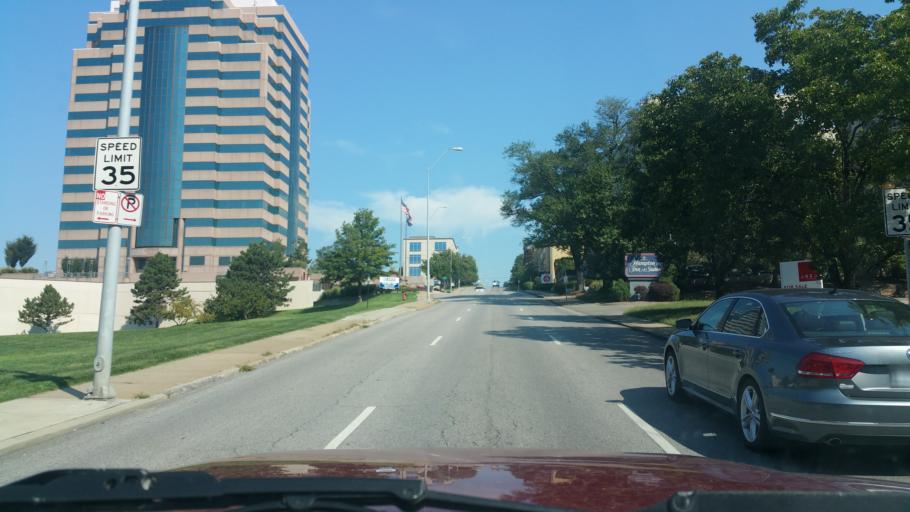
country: US
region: Kansas
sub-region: Johnson County
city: Westwood
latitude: 39.0429
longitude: -94.5974
